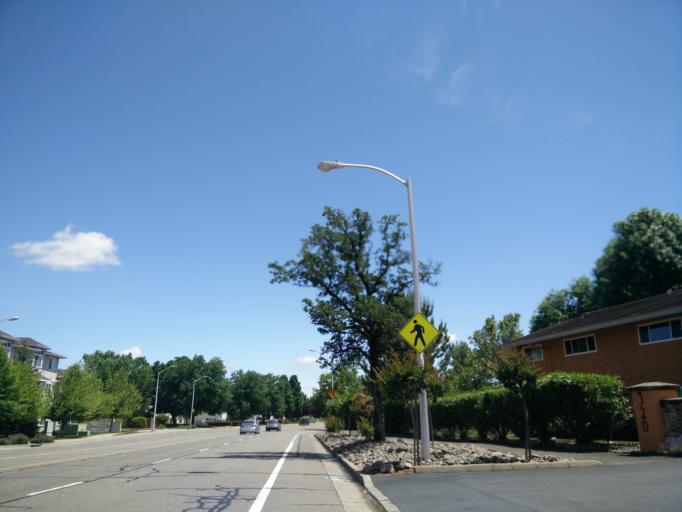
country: US
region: California
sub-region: Shasta County
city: Redding
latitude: 40.6006
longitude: -122.3728
